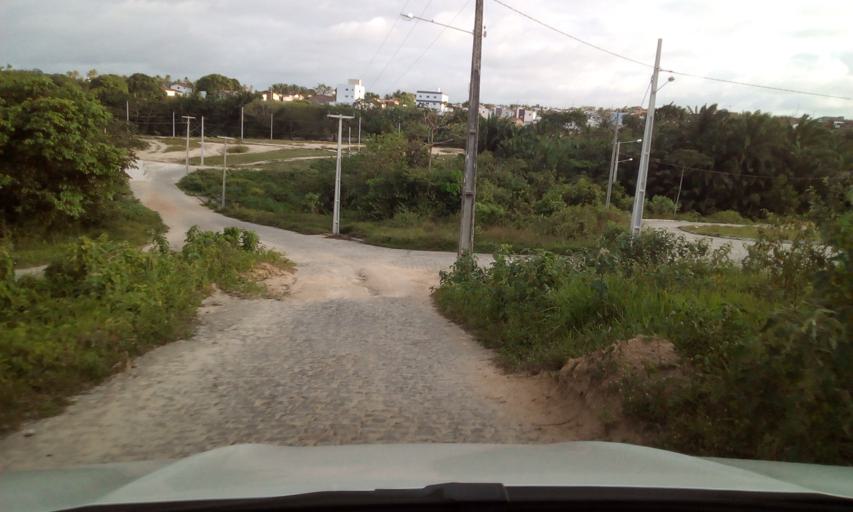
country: BR
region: Paraiba
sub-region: Joao Pessoa
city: Joao Pessoa
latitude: -7.1894
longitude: -34.8784
